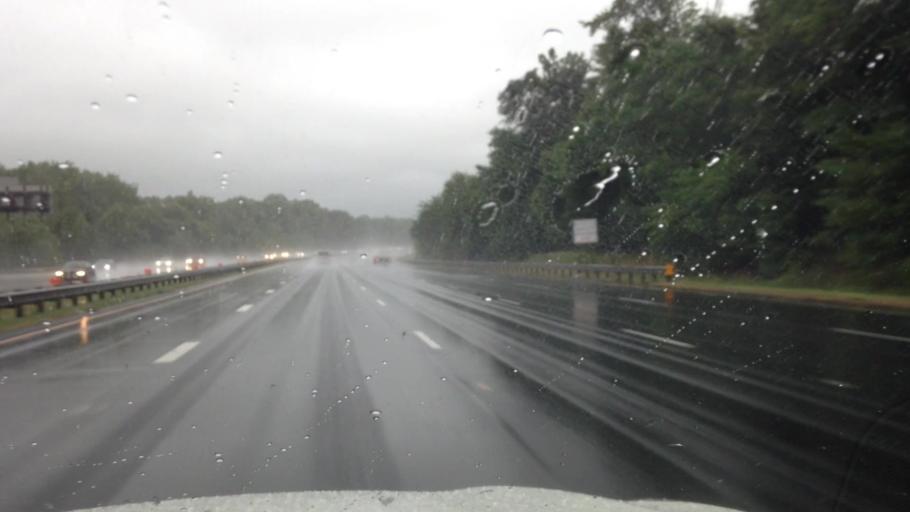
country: US
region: Maryland
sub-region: Prince George's County
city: Bowie
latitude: 38.9485
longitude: -76.7556
